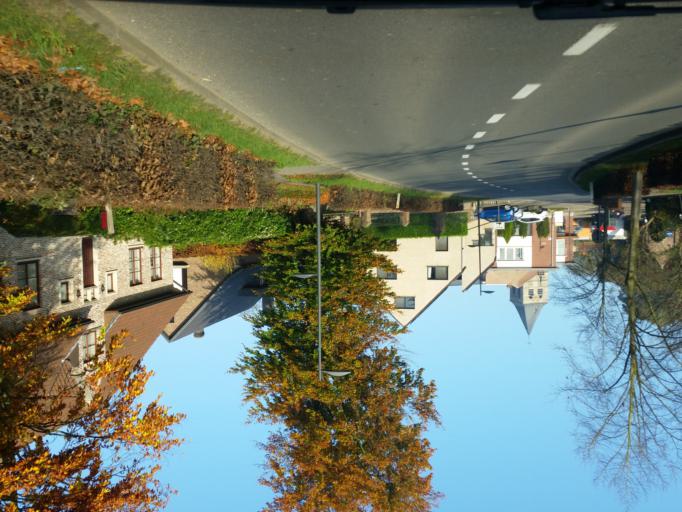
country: BE
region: Flanders
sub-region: Provincie Oost-Vlaanderen
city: Denderleeuw
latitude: 50.9462
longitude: 4.1017
